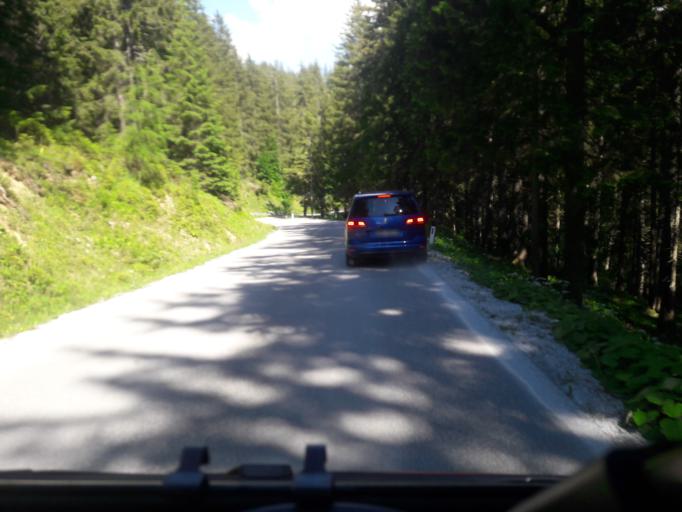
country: AT
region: Styria
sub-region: Politischer Bezirk Liezen
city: Tauplitz
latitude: 47.5827
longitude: 13.9602
